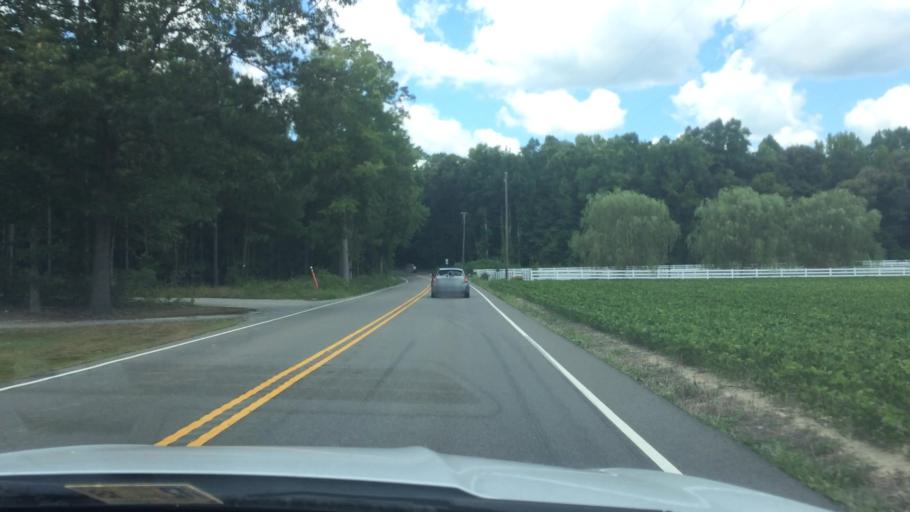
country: US
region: Virginia
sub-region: King William County
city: West Point
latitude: 37.6036
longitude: -76.7708
